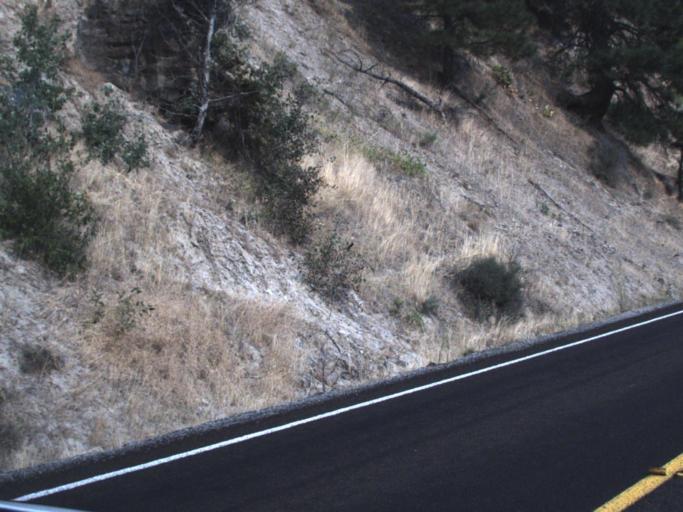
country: US
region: Washington
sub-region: Kittitas County
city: Cle Elum
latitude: 47.1340
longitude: -120.7859
